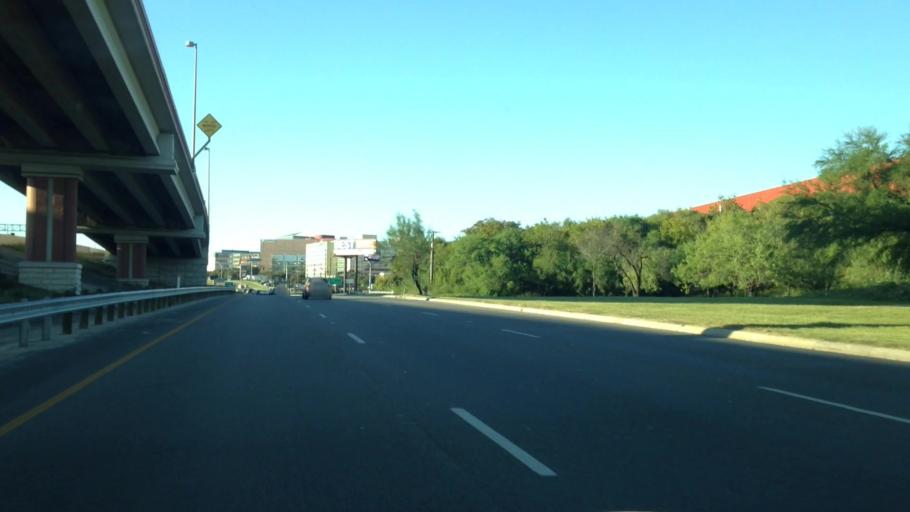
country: US
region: Texas
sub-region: Bexar County
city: Castle Hills
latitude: 29.5254
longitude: -98.4820
